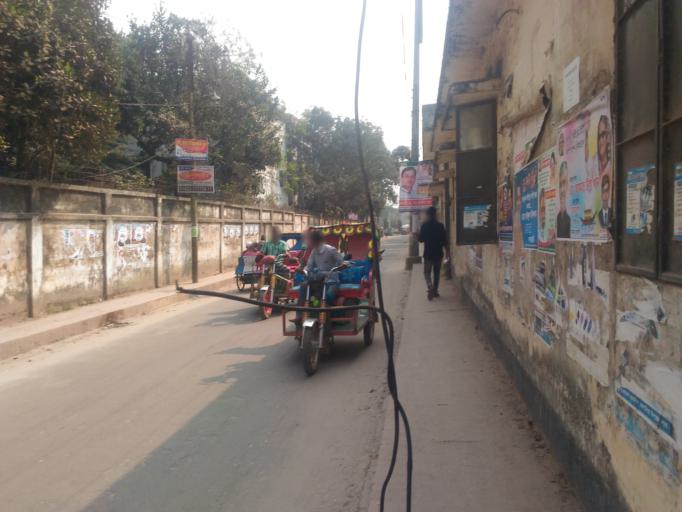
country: BD
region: Dhaka
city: Tungi
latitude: 24.0009
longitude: 90.4260
